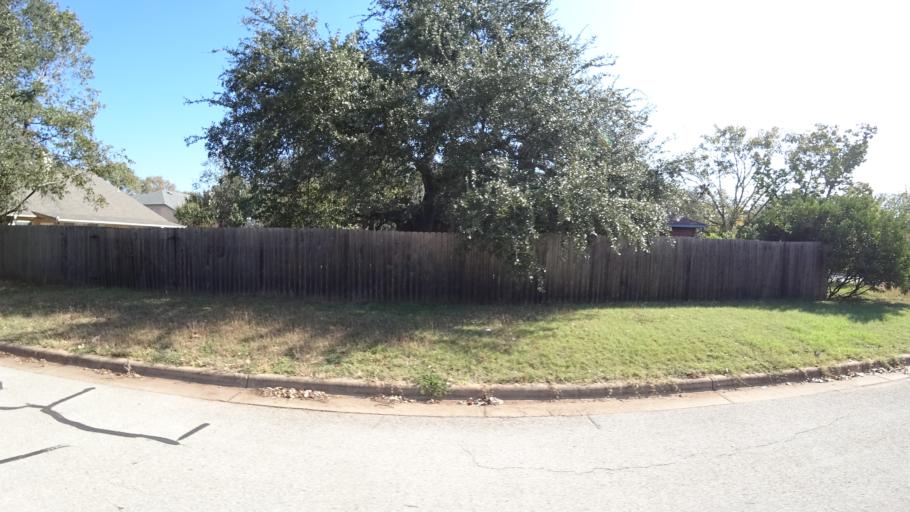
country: US
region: Texas
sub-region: Travis County
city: Shady Hollow
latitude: 30.1697
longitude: -97.8703
